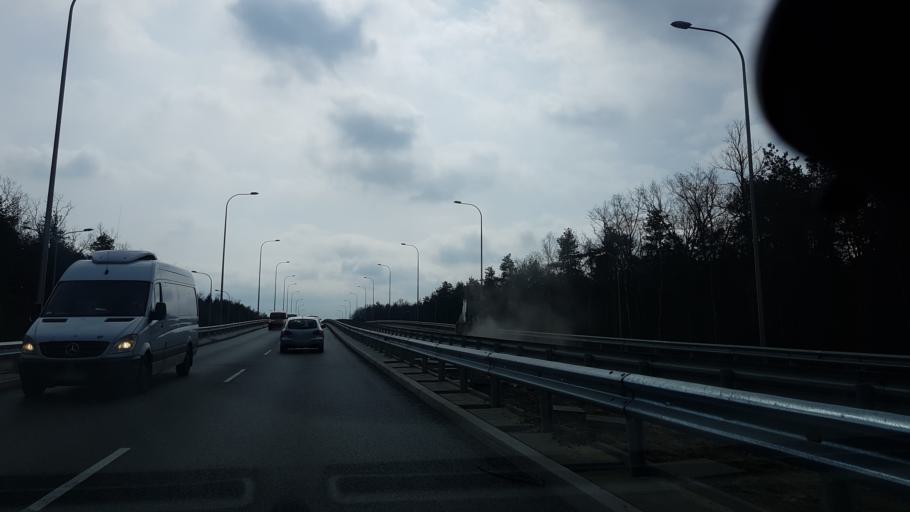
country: PL
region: Masovian Voivodeship
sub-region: Warszawa
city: Rembertow
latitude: 52.2711
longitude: 21.1436
